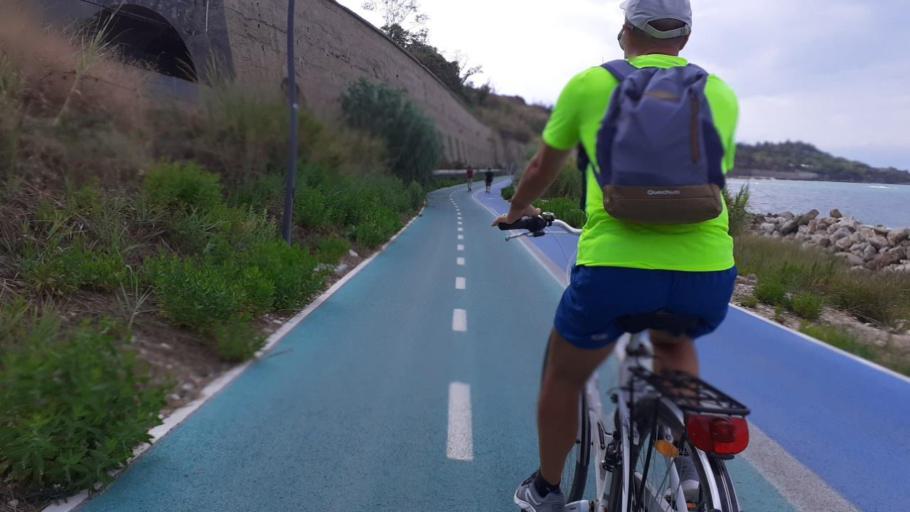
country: IT
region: Abruzzo
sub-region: Provincia di Chieti
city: Ortona
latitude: 42.3603
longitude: 14.4057
